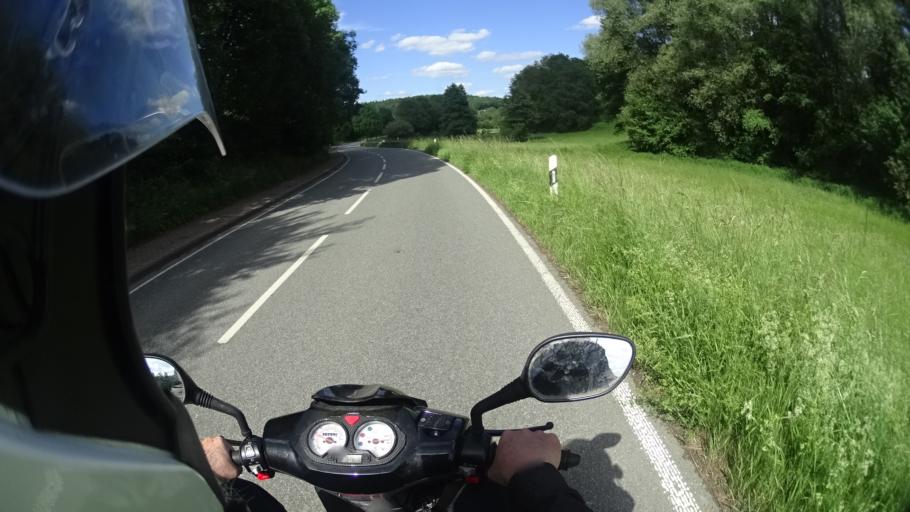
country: DE
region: Hesse
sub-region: Regierungsbezirk Darmstadt
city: Schlangenbad
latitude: 50.1049
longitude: 8.0784
